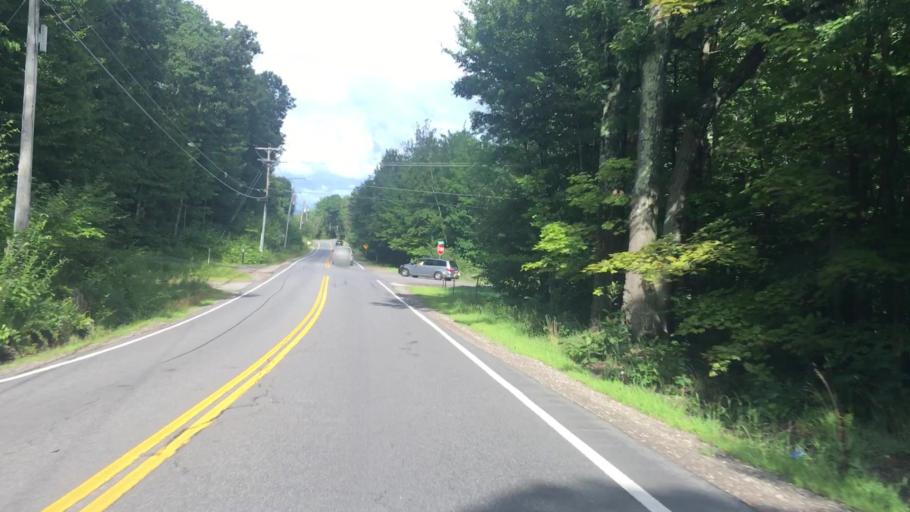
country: US
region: New Hampshire
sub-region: Belknap County
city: Gilford
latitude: 43.5634
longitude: -71.3752
